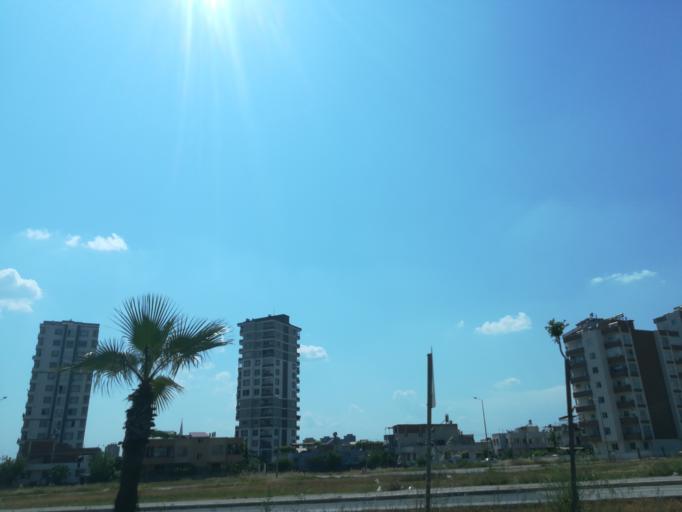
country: TR
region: Adana
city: Yuregir
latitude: 37.0159
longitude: 35.3994
